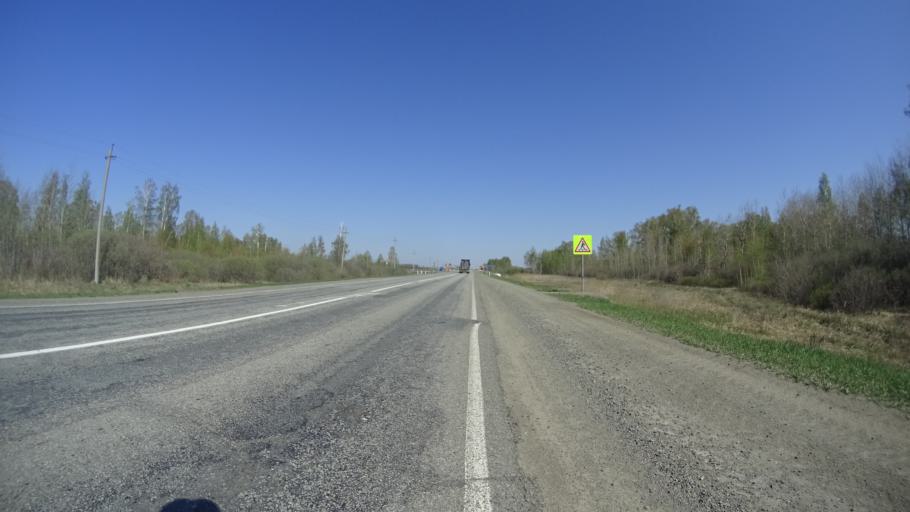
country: RU
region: Chelyabinsk
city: Troitsk
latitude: 54.1855
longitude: 61.4342
